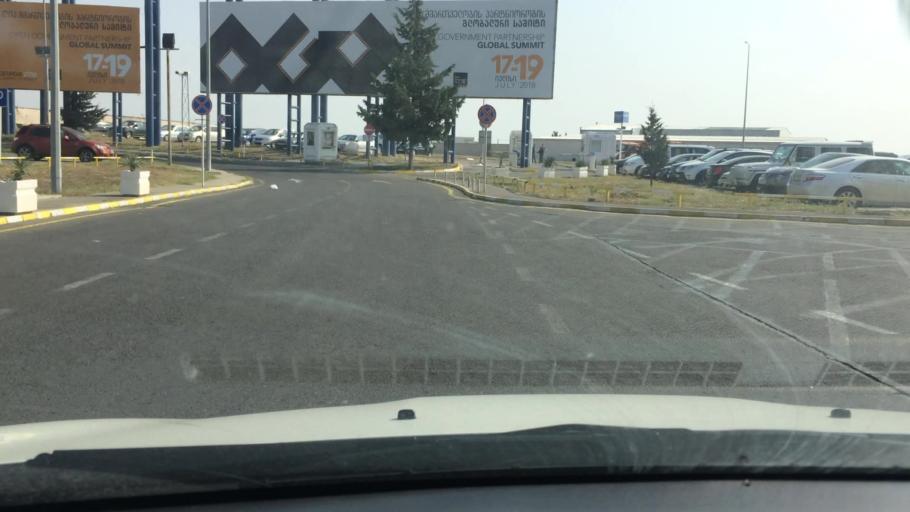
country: GE
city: Didi Lilo
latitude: 41.6694
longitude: 44.9656
